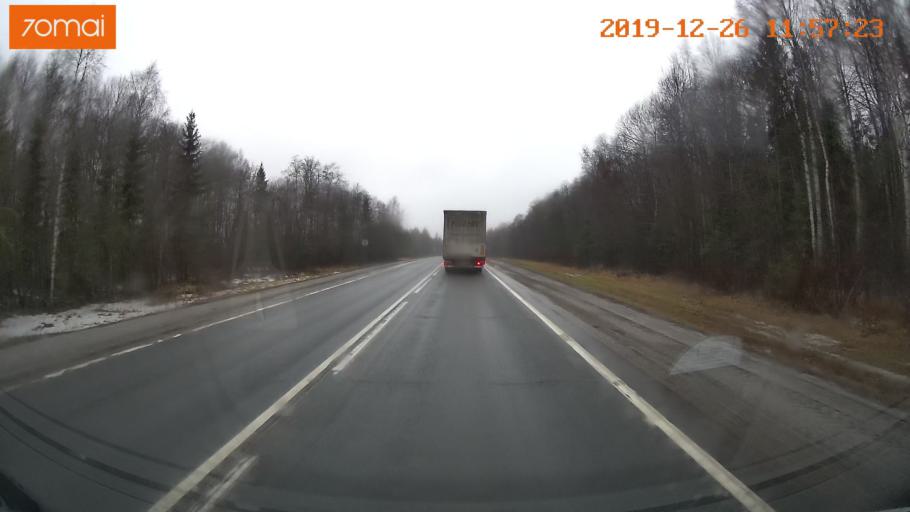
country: RU
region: Vologda
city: Sheksna
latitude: 59.2887
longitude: 38.2510
